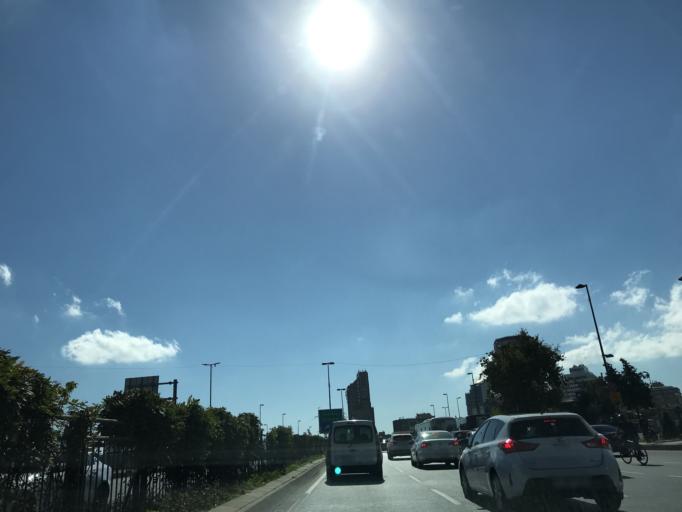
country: TR
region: Istanbul
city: Sisli
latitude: 41.0676
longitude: 29.0137
